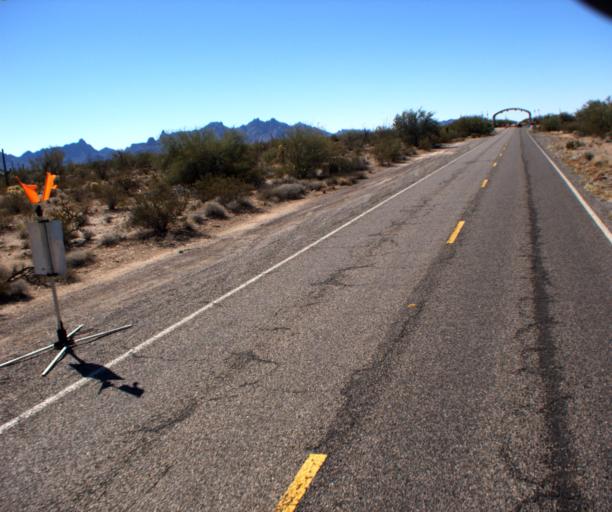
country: US
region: Arizona
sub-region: Pima County
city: Ajo
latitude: 32.2054
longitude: -112.7588
